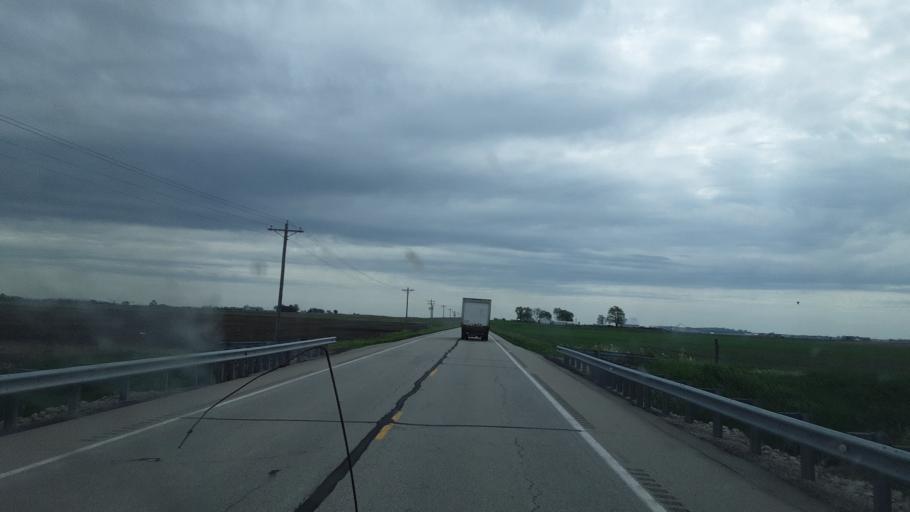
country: US
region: Illinois
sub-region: Mason County
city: Mason City
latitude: 40.3038
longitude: -89.7623
